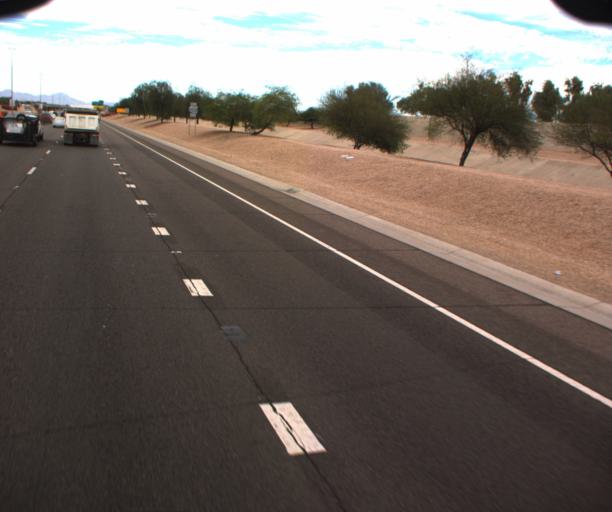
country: US
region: Arizona
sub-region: Maricopa County
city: Chandler
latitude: 33.2874
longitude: -111.8489
